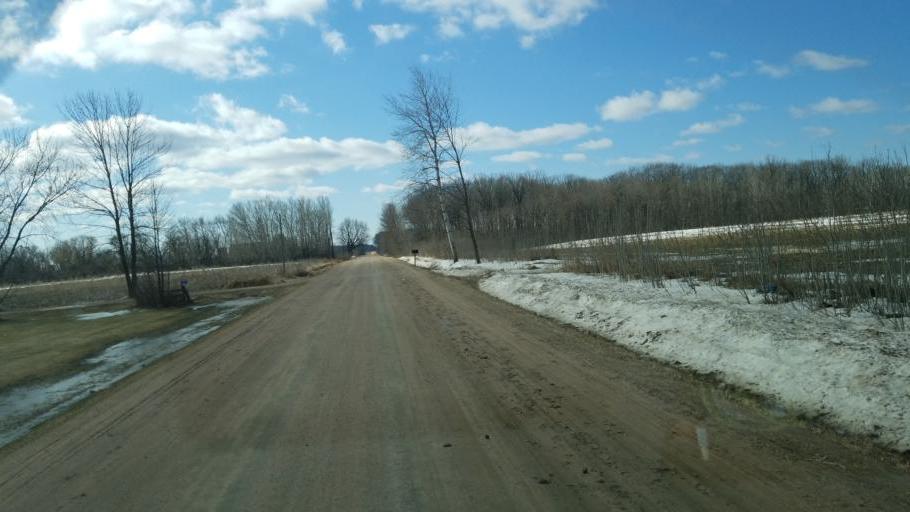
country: US
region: Wisconsin
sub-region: Clark County
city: Loyal
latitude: 44.6373
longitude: -90.3973
